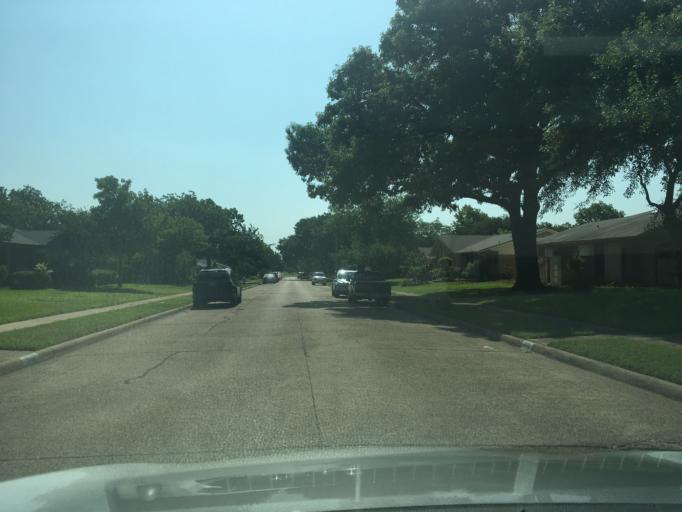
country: US
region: Texas
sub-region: Dallas County
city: Richardson
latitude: 32.9251
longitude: -96.6871
